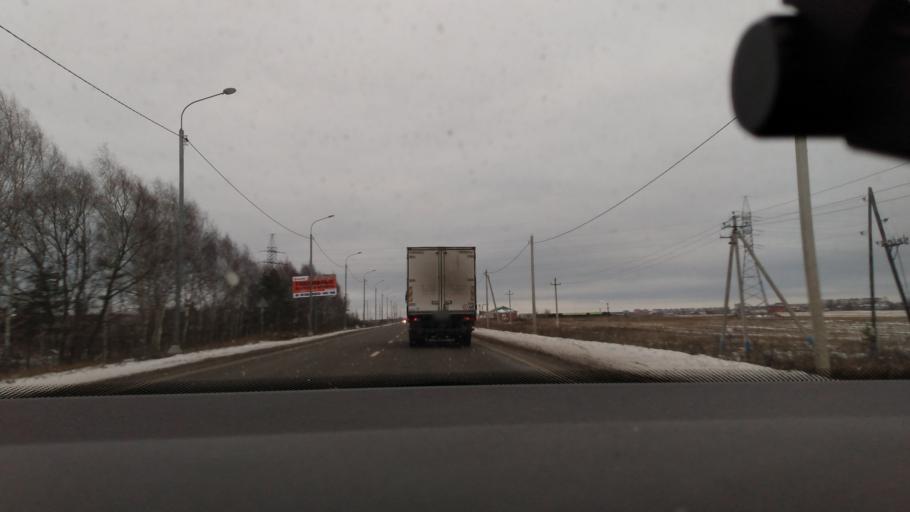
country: RU
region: Moskovskaya
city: Yegor'yevsk
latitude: 55.4073
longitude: 39.0536
